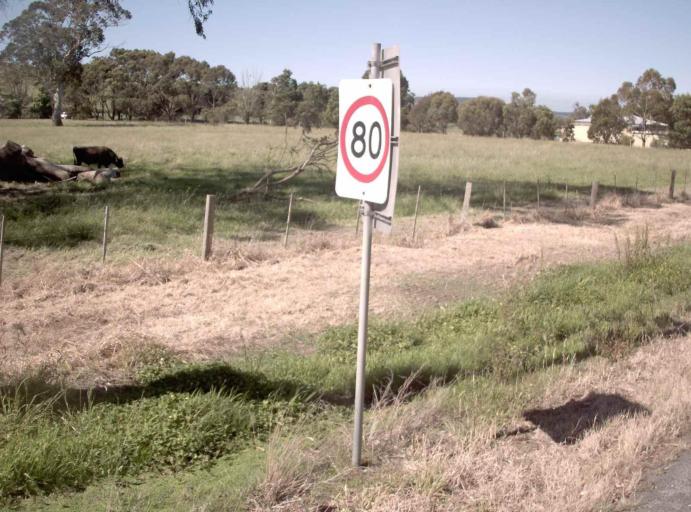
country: AU
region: Victoria
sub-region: Latrobe
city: Morwell
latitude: -38.6647
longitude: 146.4411
